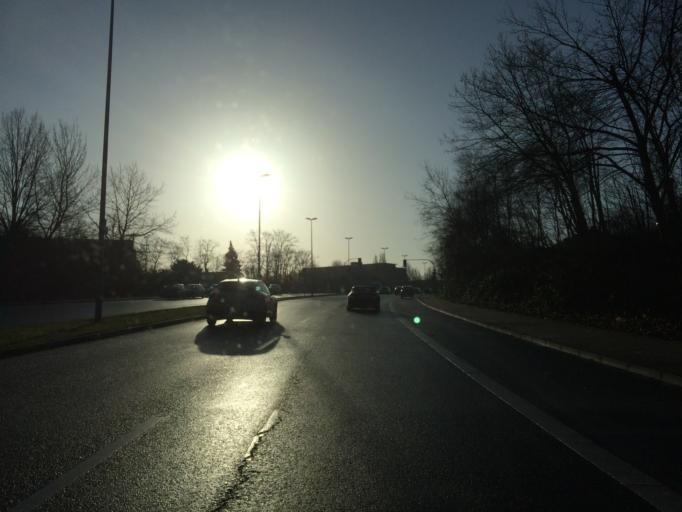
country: DE
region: North Rhine-Westphalia
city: Bochum-Hordel
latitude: 51.5365
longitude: 7.1831
